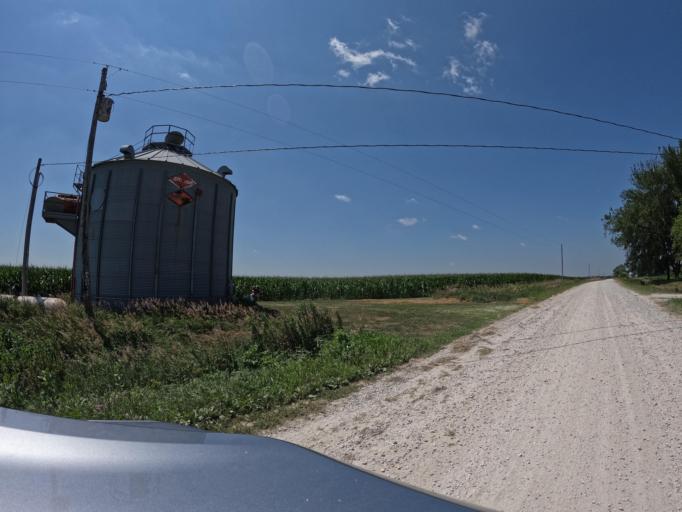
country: US
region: Iowa
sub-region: Keokuk County
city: Sigourney
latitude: 41.2885
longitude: -92.2310
